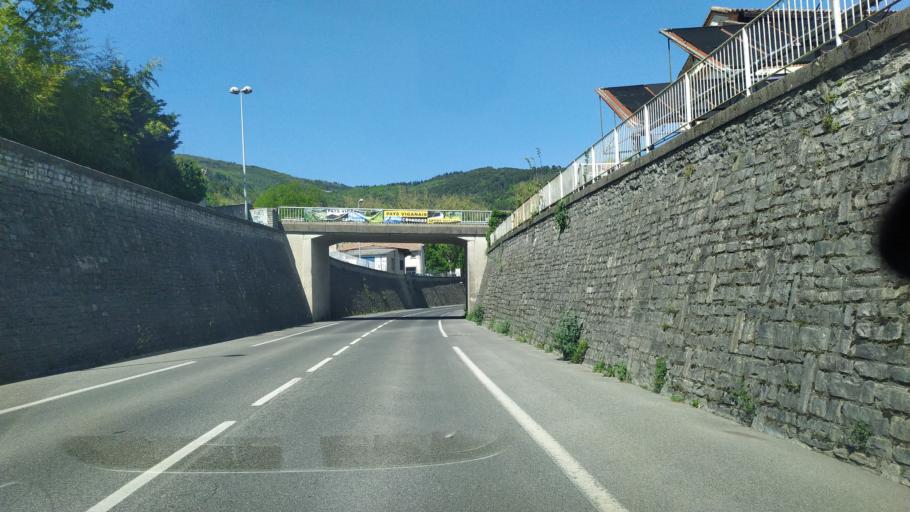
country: FR
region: Languedoc-Roussillon
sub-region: Departement du Gard
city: Le Vigan
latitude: 43.9882
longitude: 3.6048
